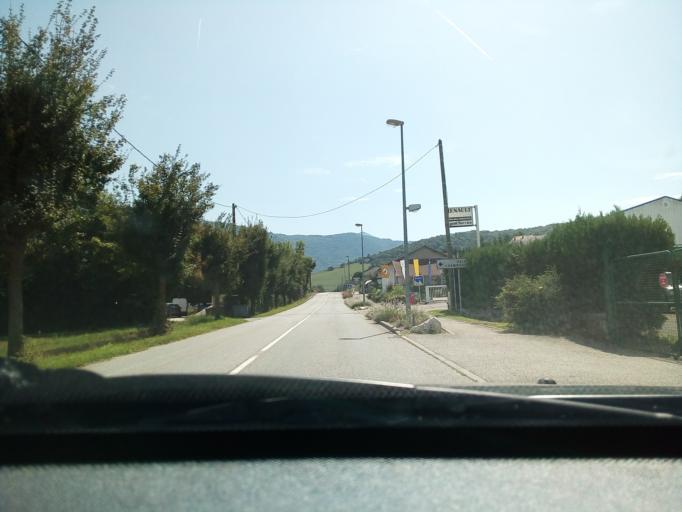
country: FR
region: Rhone-Alpes
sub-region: Departement de l'Isere
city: Brie-et-Angonnes
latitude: 45.1162
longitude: 5.7836
